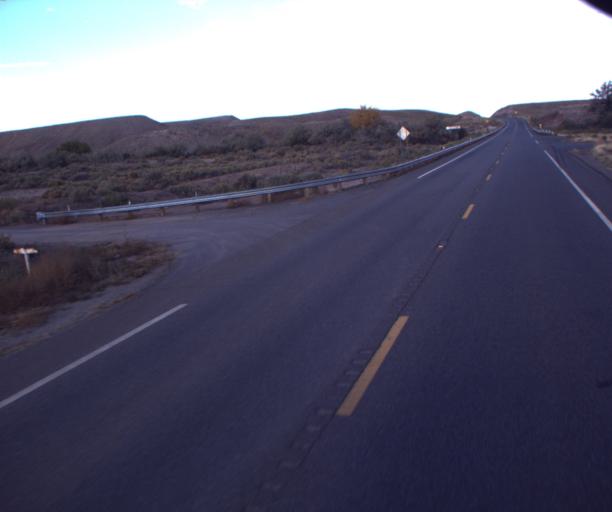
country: US
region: New Mexico
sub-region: San Juan County
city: Shiprock
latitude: 36.9325
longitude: -109.1081
